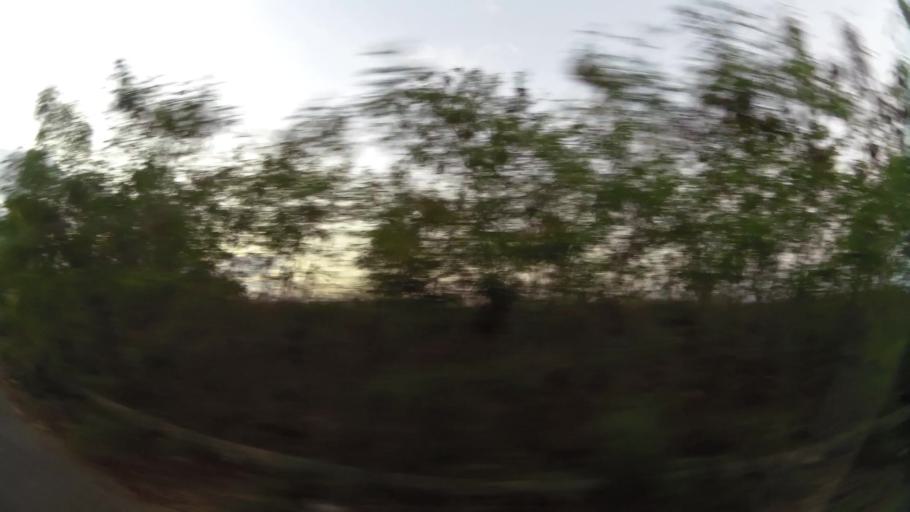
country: DO
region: Nacional
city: La Agustina
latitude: 18.5428
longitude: -69.9461
